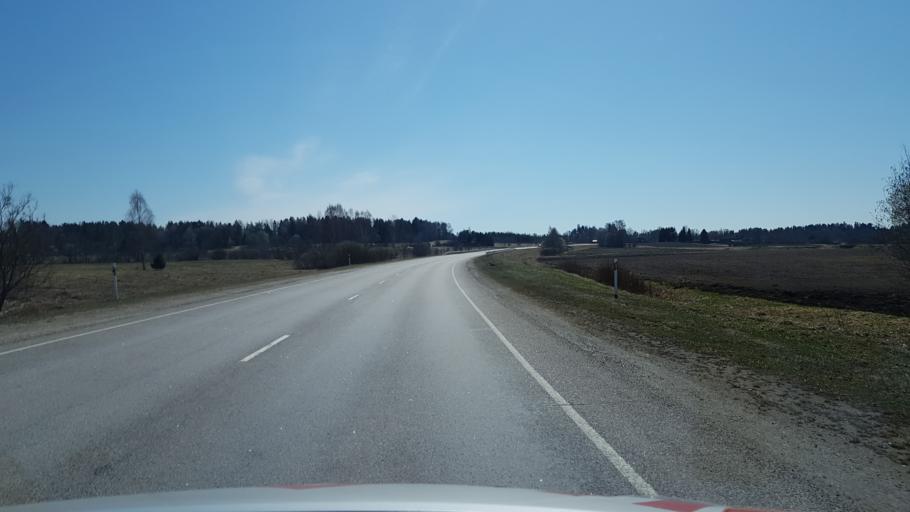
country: EE
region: Ida-Virumaa
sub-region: Johvi vald
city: Johvi
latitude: 59.1517
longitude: 27.3591
